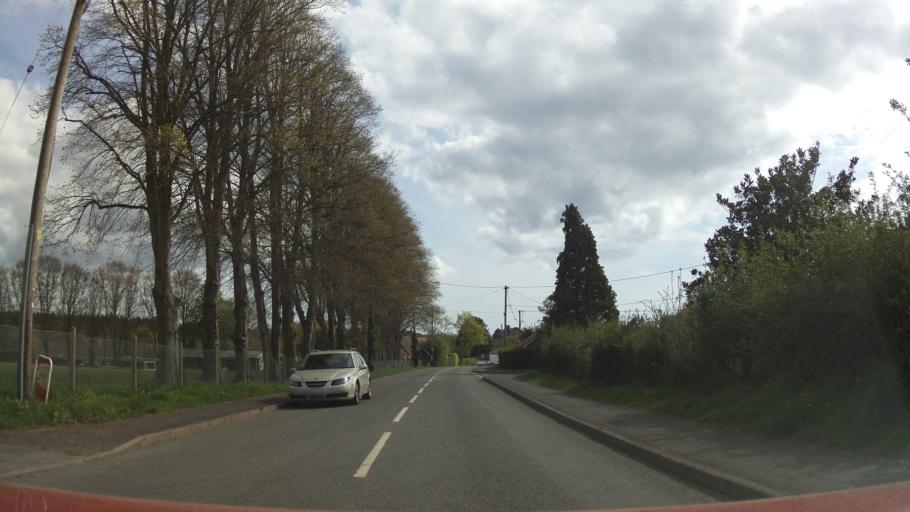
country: GB
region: England
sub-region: Hampshire
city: Romsey
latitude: 51.0228
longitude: -1.4661
